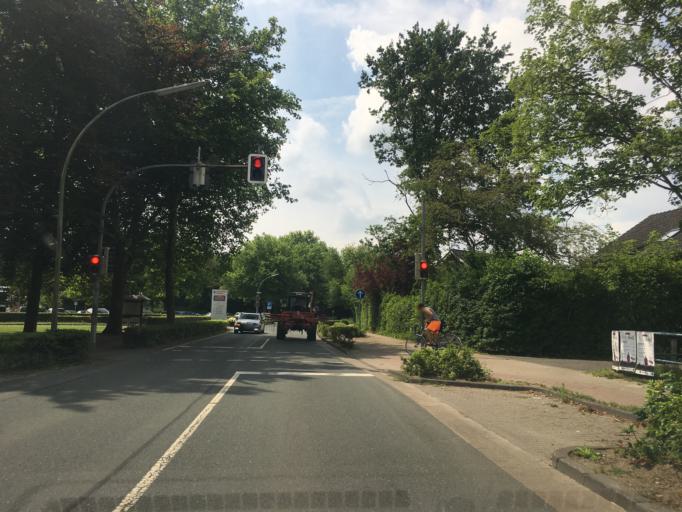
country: DE
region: North Rhine-Westphalia
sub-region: Regierungsbezirk Munster
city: Senden
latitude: 51.8555
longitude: 7.4766
